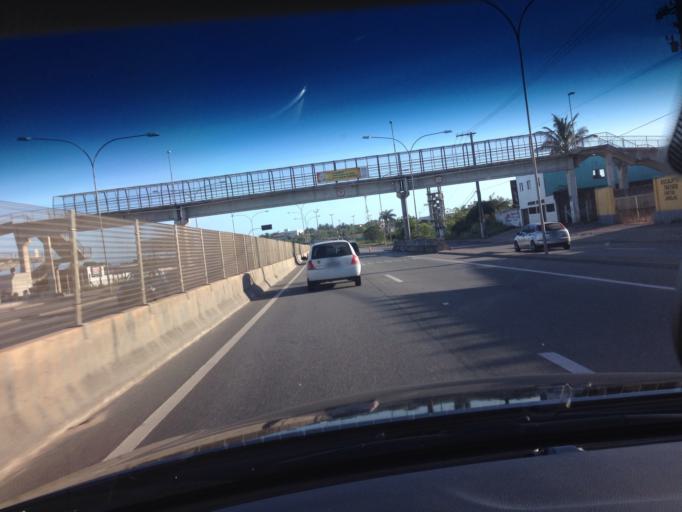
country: BR
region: Espirito Santo
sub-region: Viana
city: Viana
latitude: -20.5108
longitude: -40.3639
